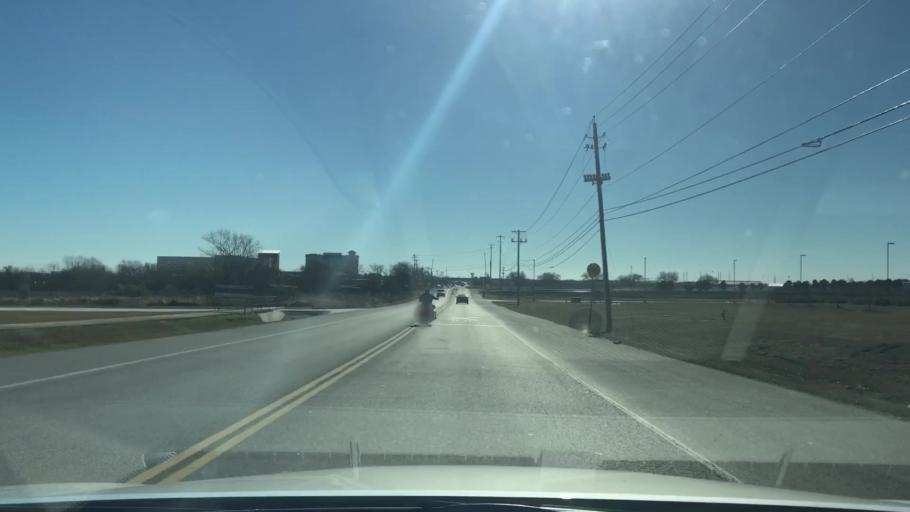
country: US
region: Texas
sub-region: Hays County
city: San Marcos
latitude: 29.8462
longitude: -97.9779
